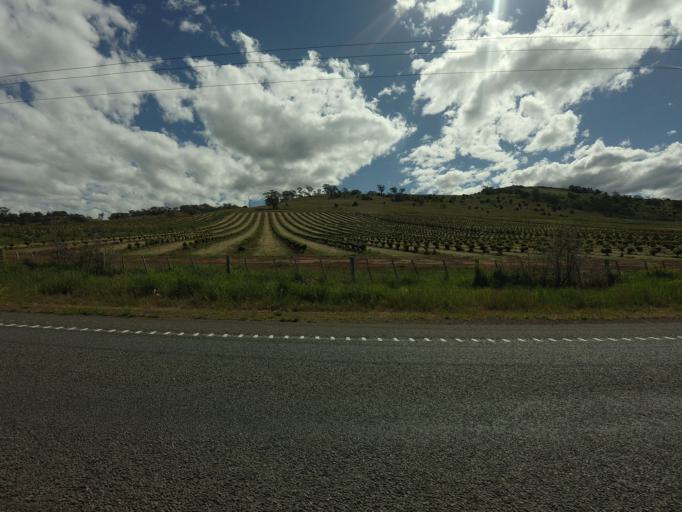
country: AU
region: Tasmania
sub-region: Northern Midlands
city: Evandale
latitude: -42.0561
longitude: 147.4826
